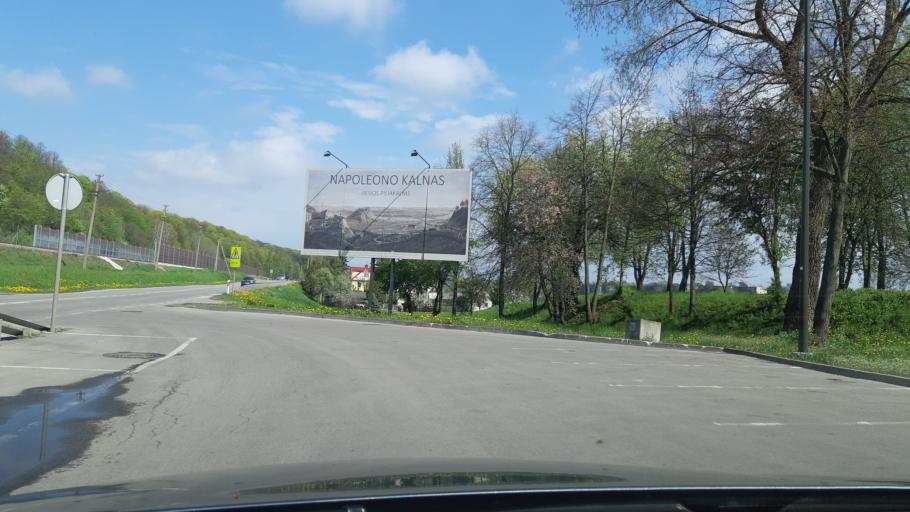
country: LT
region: Kauno apskritis
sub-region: Kaunas
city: Aleksotas
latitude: 54.8619
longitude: 23.9261
